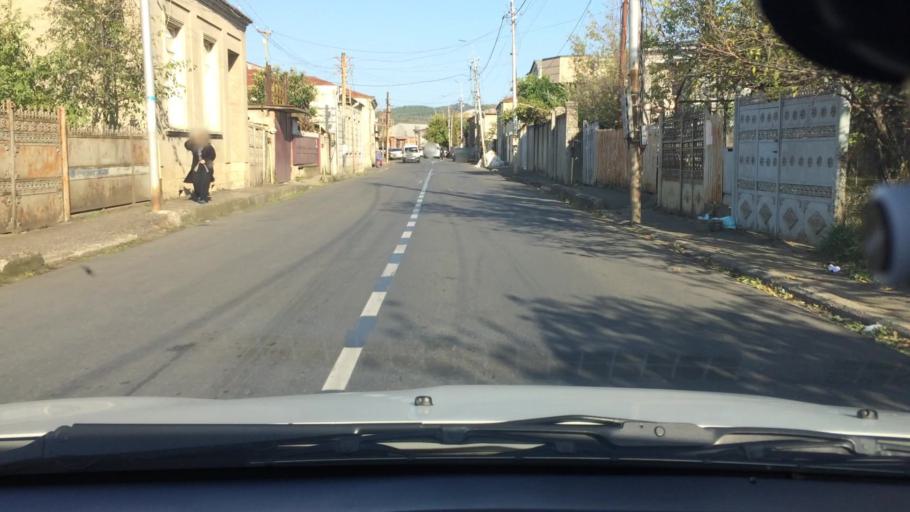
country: GE
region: Imereti
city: Kutaisi
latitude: 42.2709
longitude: 42.7133
